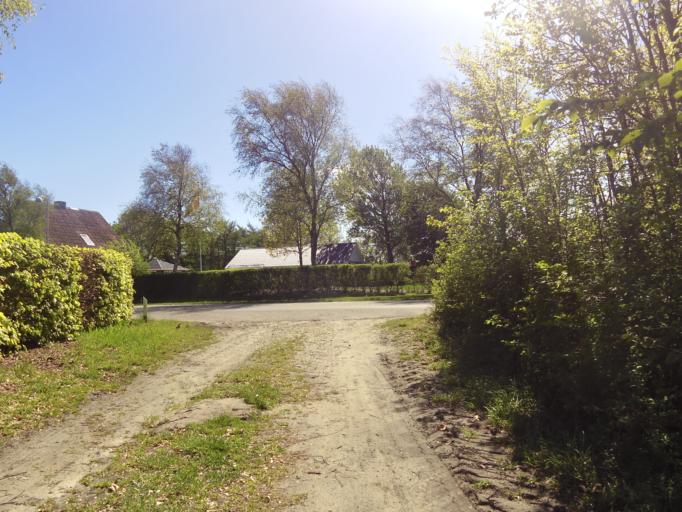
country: DK
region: South Denmark
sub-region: Tonder Kommune
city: Sherrebek
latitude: 55.2307
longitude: 8.7330
